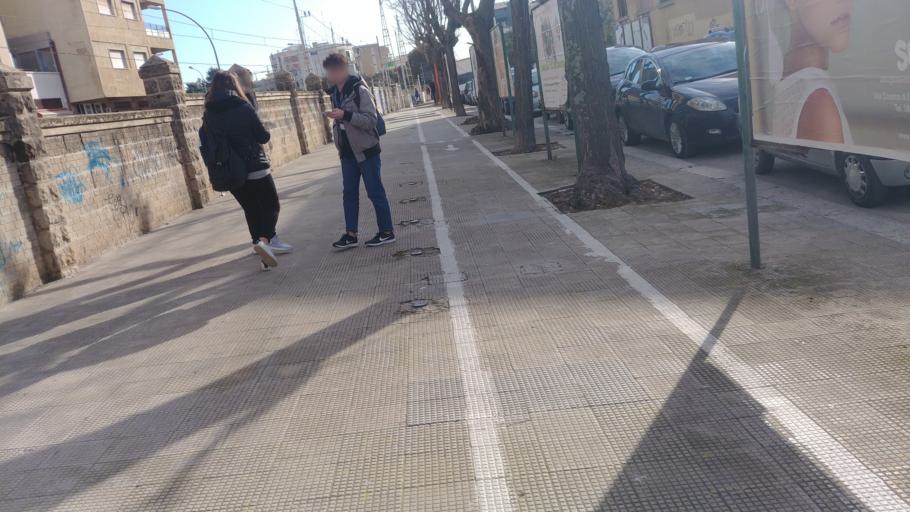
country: IT
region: Apulia
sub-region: Provincia di Barletta - Andria - Trani
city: Andria
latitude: 41.2315
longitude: 16.3032
